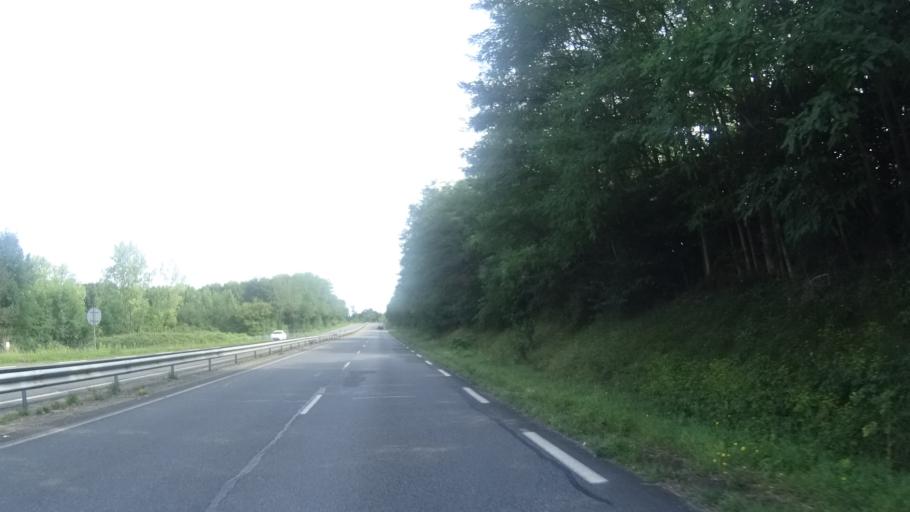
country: FR
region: Aquitaine
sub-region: Departement de la Dordogne
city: Neuvic
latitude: 45.0774
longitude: 0.4518
